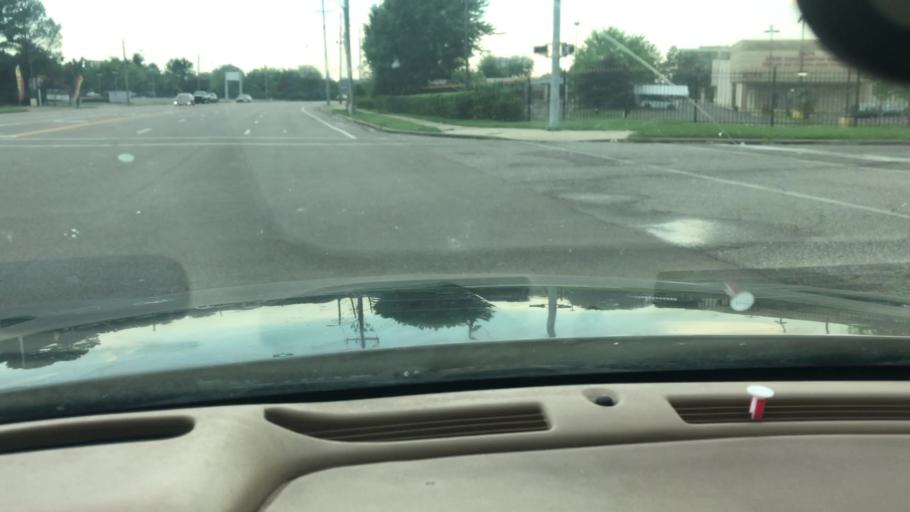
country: US
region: Tennessee
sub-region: Shelby County
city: Germantown
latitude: 35.0747
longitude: -89.9018
